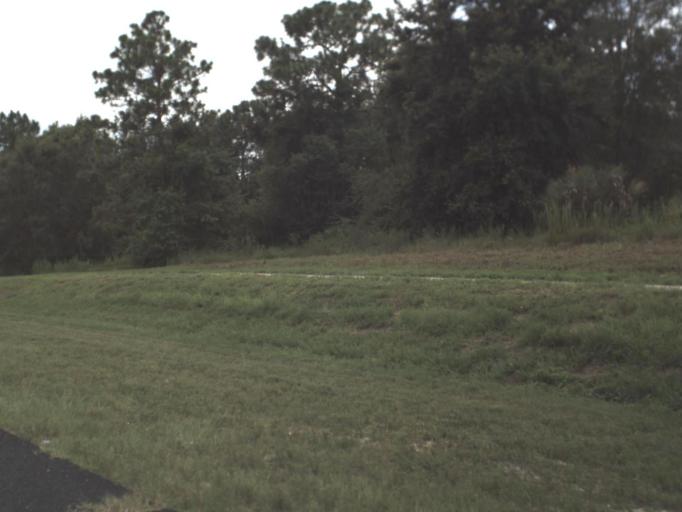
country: US
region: Florida
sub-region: Citrus County
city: Lecanto
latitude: 28.8721
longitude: -82.5166
